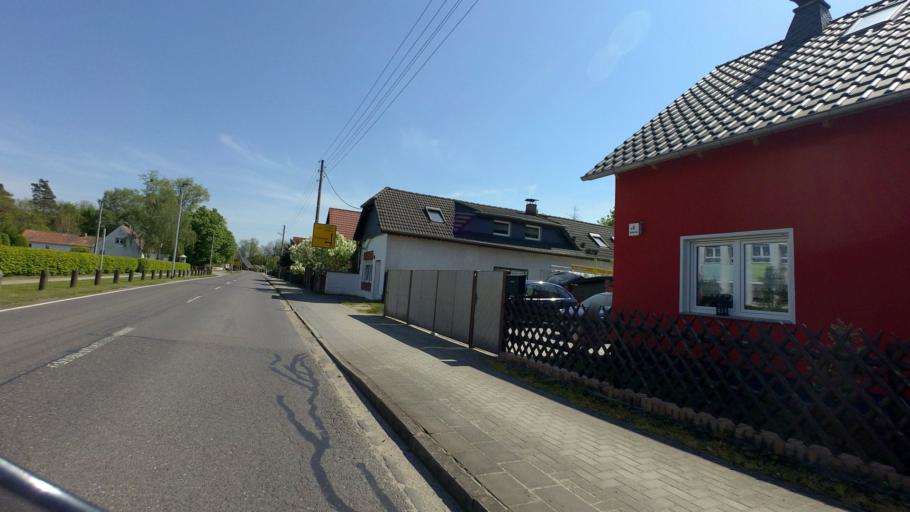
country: DE
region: Brandenburg
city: Schlepzig
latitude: 52.0534
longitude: 13.9890
